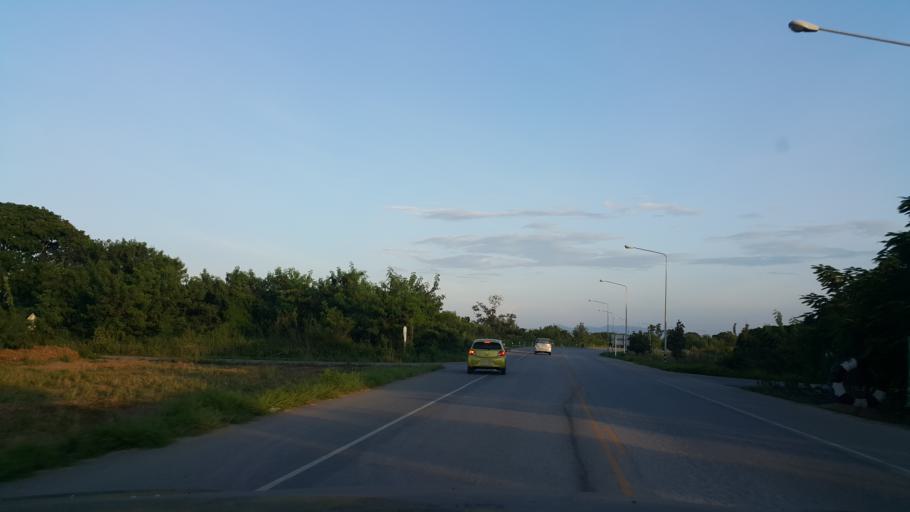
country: TH
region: Lamphun
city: Pa Sang
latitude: 18.5241
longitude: 98.8736
